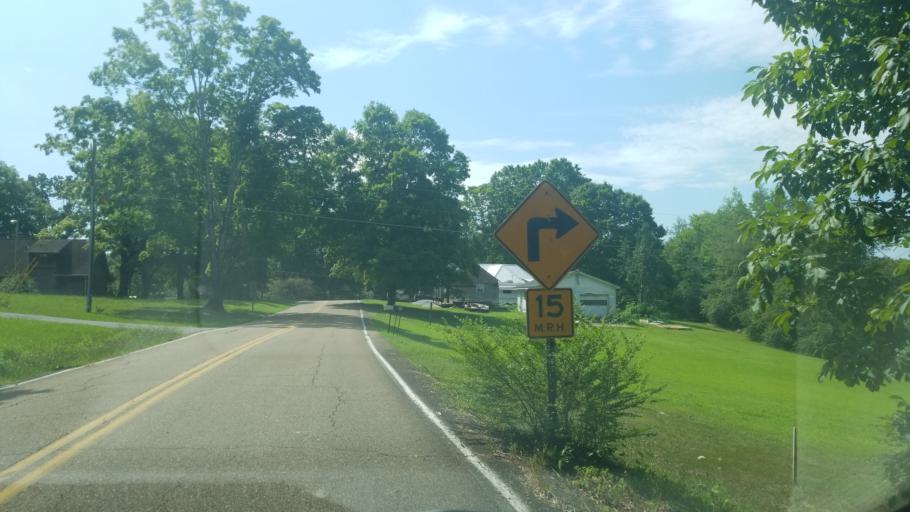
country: US
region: Tennessee
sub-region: Hamilton County
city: Lakesite
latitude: 35.1755
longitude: -85.0622
